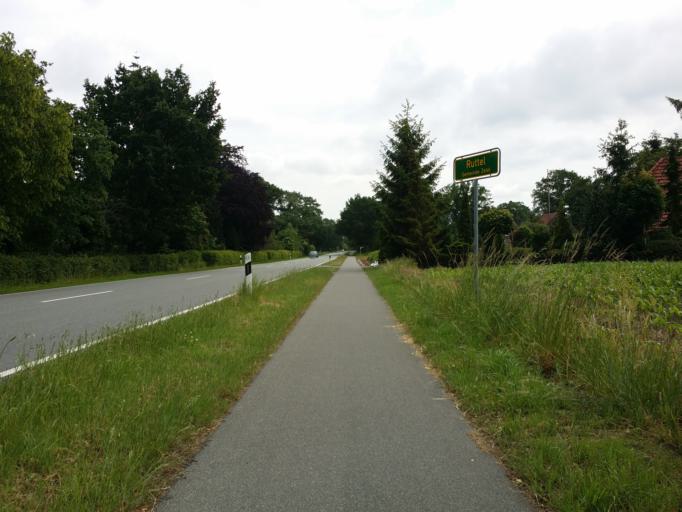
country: DE
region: Lower Saxony
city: Zetel
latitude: 53.3972
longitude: 7.9234
